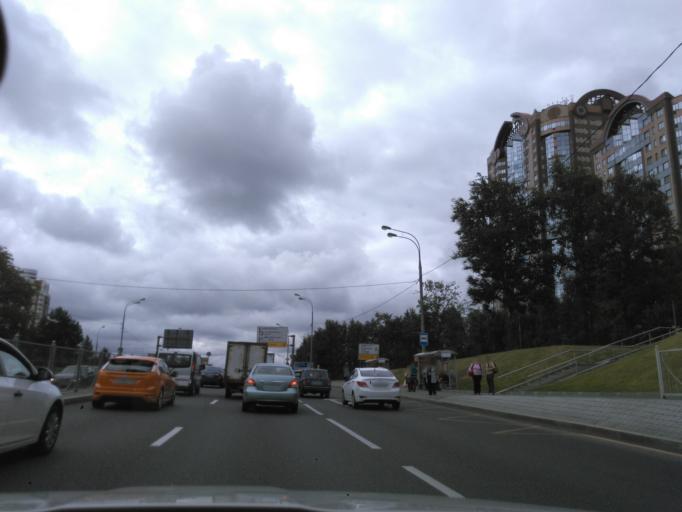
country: RU
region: Moscow
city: Davydkovo
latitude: 55.7261
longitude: 37.4479
